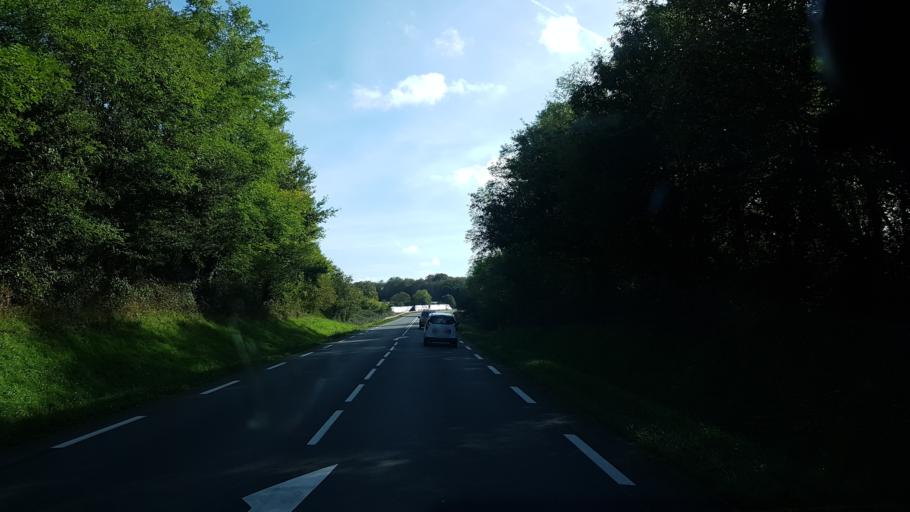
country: FR
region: Poitou-Charentes
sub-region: Departement de la Charente
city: Saint-Claud
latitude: 45.8642
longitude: 0.4666
